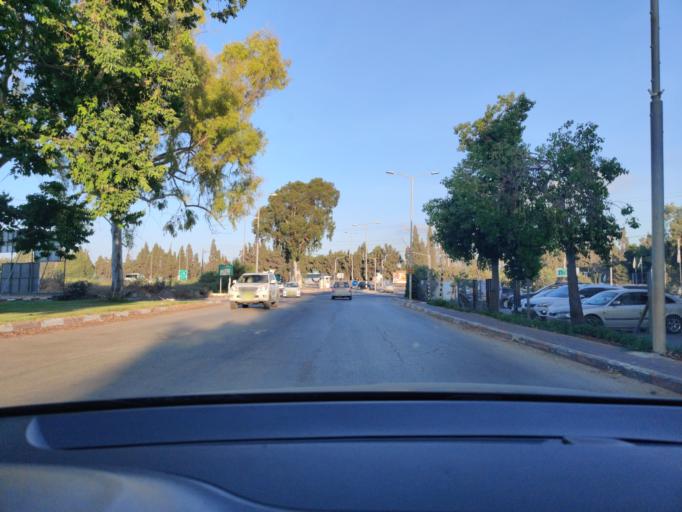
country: IL
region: Central District
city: Elyakhin
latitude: 32.4482
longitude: 34.9561
